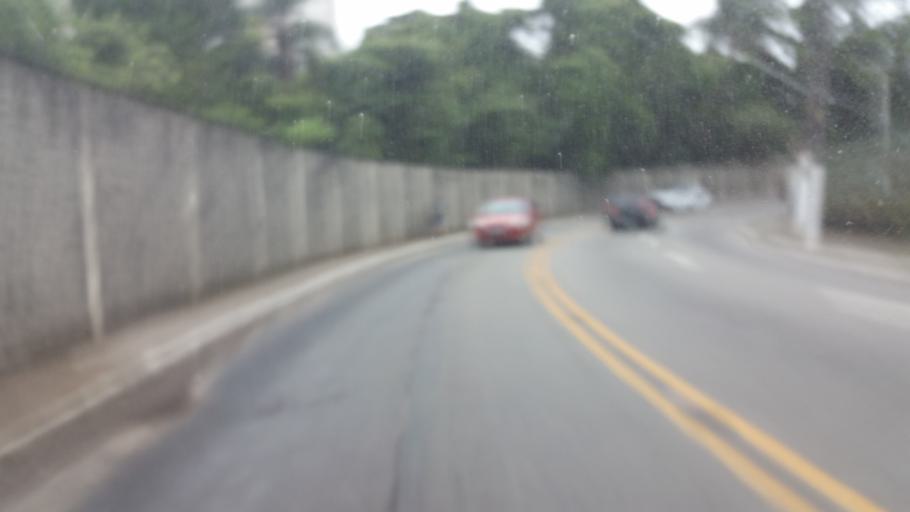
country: BR
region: Sao Paulo
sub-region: Diadema
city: Diadema
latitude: -23.6565
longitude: -46.6166
